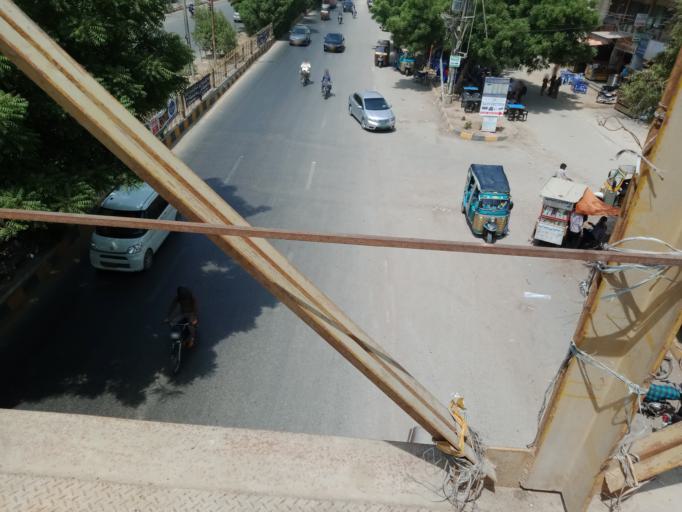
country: PK
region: Sindh
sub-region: Karachi District
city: Karachi
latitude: 24.9295
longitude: 67.1157
